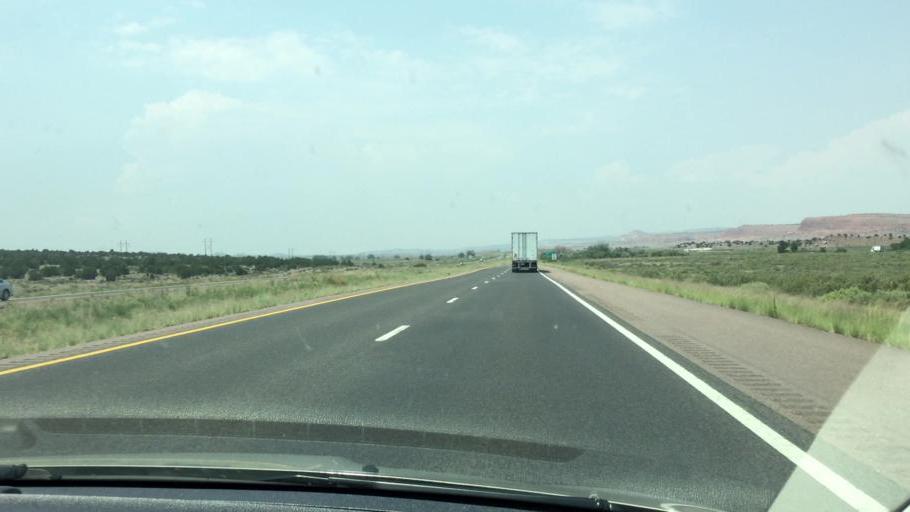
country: US
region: New Mexico
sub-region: McKinley County
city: Church Rock
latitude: 35.4951
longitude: -108.4975
